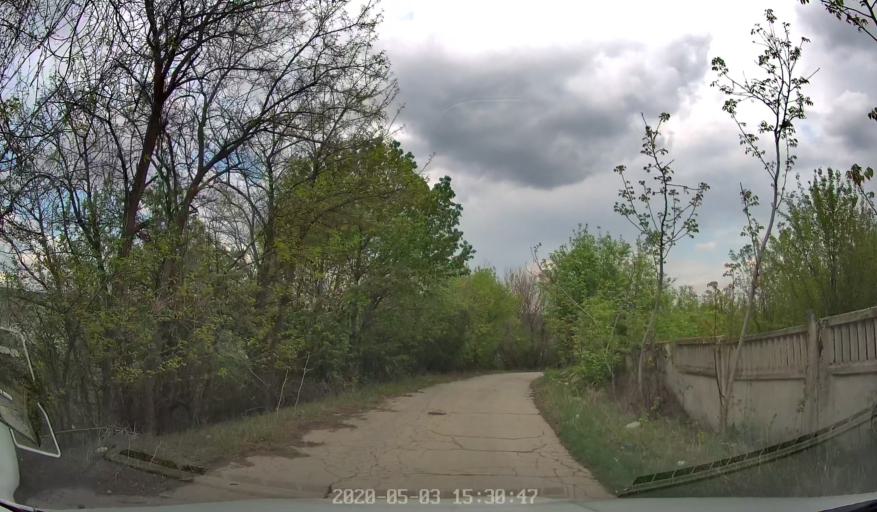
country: MD
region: Chisinau
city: Vatra
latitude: 47.0980
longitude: 28.7046
